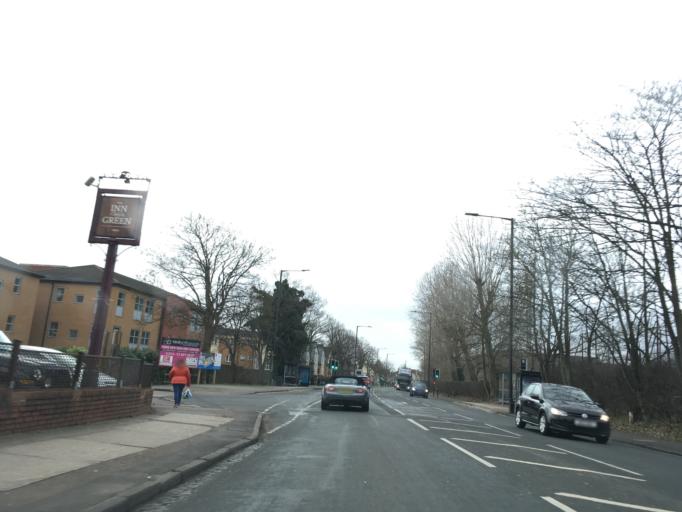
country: GB
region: England
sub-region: Bristol
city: Bristol
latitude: 51.4945
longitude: -2.5821
